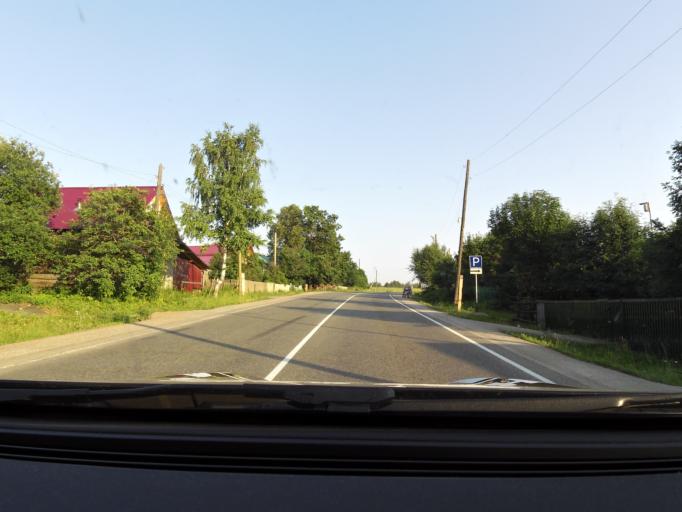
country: RU
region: Sverdlovsk
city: Nizhniye Sergi
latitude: 56.5535
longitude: 59.2160
